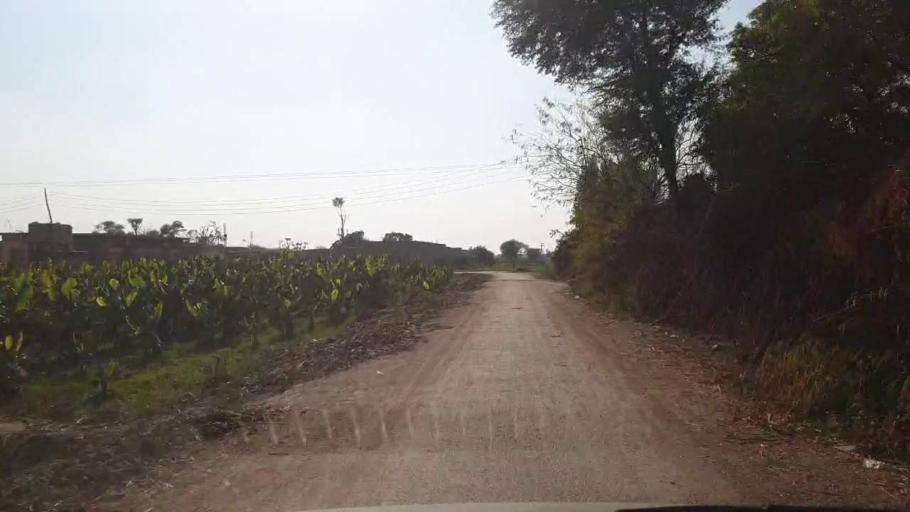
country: PK
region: Sindh
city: Chambar
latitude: 25.3377
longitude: 68.7498
